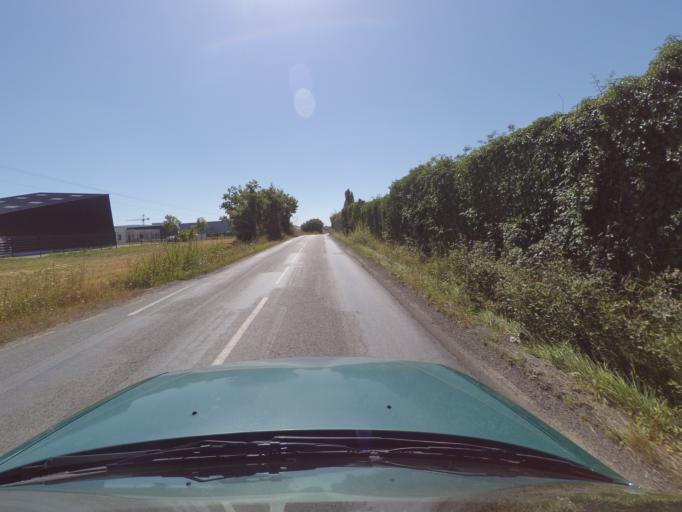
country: FR
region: Pays de la Loire
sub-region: Departement de la Loire-Atlantique
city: Le Bignon
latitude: 47.1229
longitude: -1.5090
